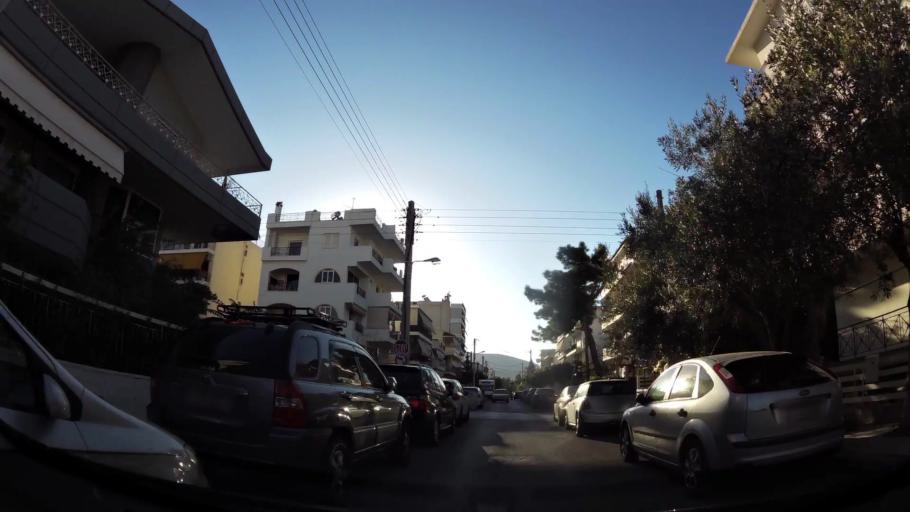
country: GR
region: Attica
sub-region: Nomarchia Athinas
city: Argyroupoli
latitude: 37.8877
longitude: 23.7569
